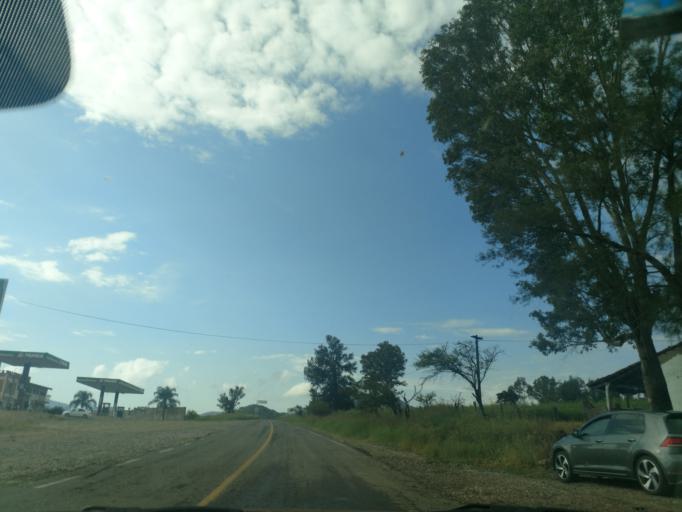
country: MX
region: Jalisco
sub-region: Atengo
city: Soyatlan del Oro
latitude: 20.5238
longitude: -104.3377
